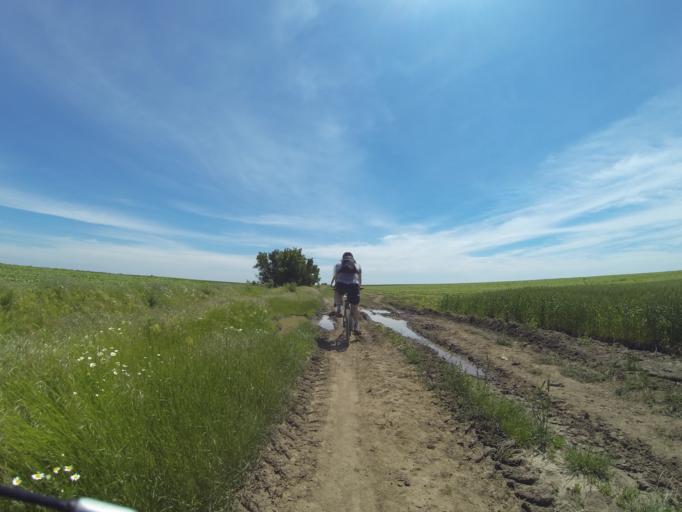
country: RO
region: Dolj
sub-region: Comuna Leu
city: Leu
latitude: 44.1878
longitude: 24.0531
